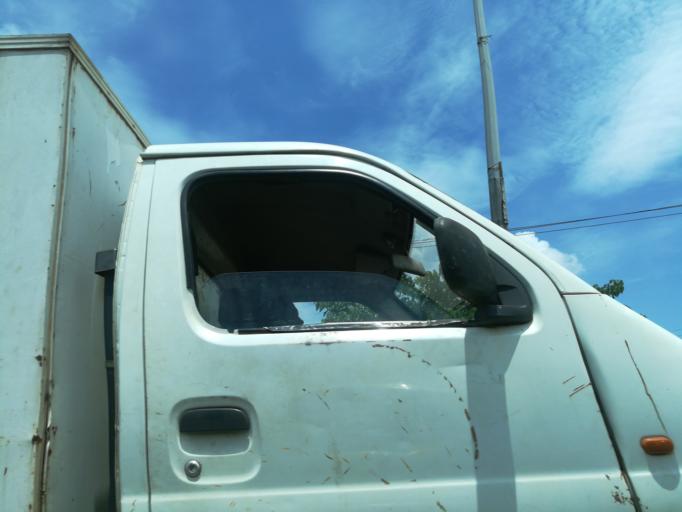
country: NG
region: Lagos
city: Ebute Ikorodu
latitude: 6.5962
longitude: 3.4936
